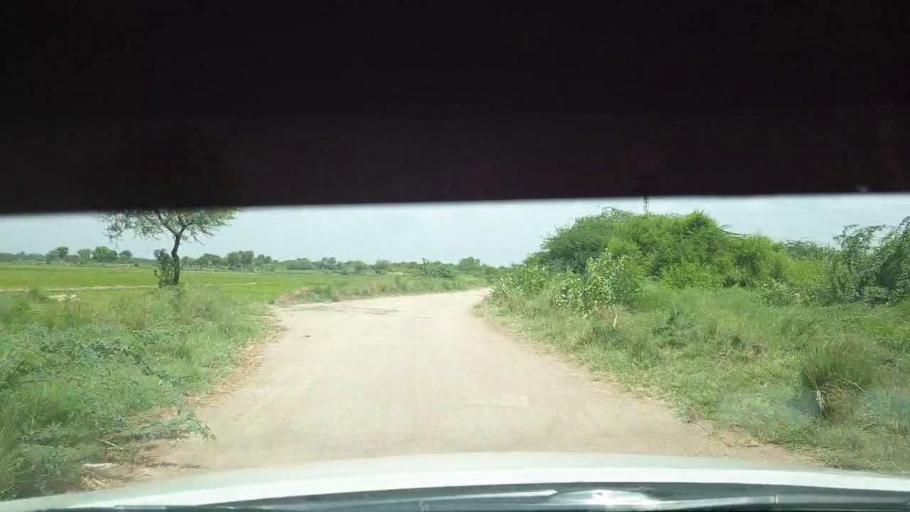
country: PK
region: Sindh
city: Kadhan
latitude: 24.5164
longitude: 68.9716
